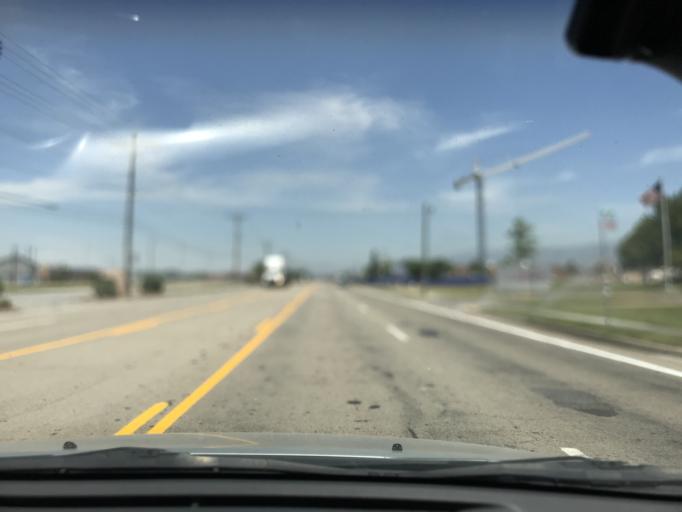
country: US
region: Utah
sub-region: Salt Lake County
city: Salt Lake City
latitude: 40.7795
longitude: -111.9535
